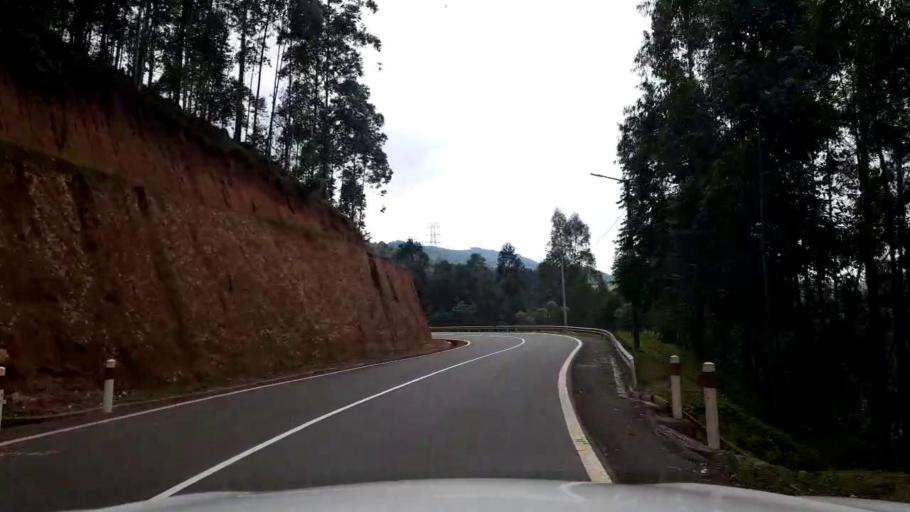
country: RW
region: Western Province
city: Kibuye
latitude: -1.9259
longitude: 29.3687
